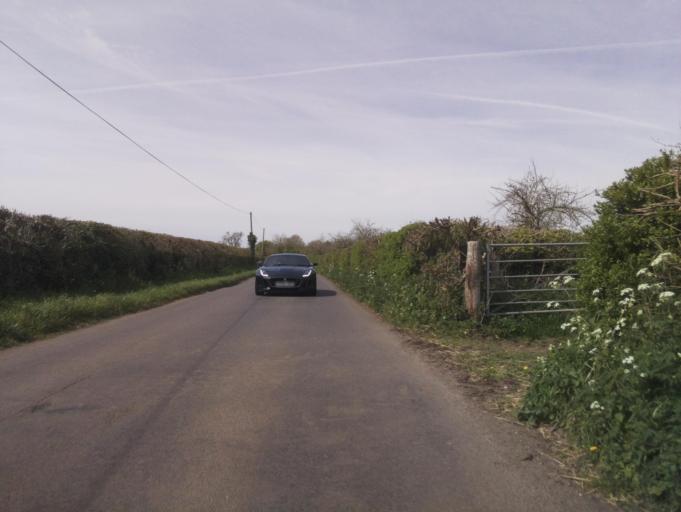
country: GB
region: England
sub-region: Somerset
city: Ilchester
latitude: 51.0160
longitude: -2.6045
